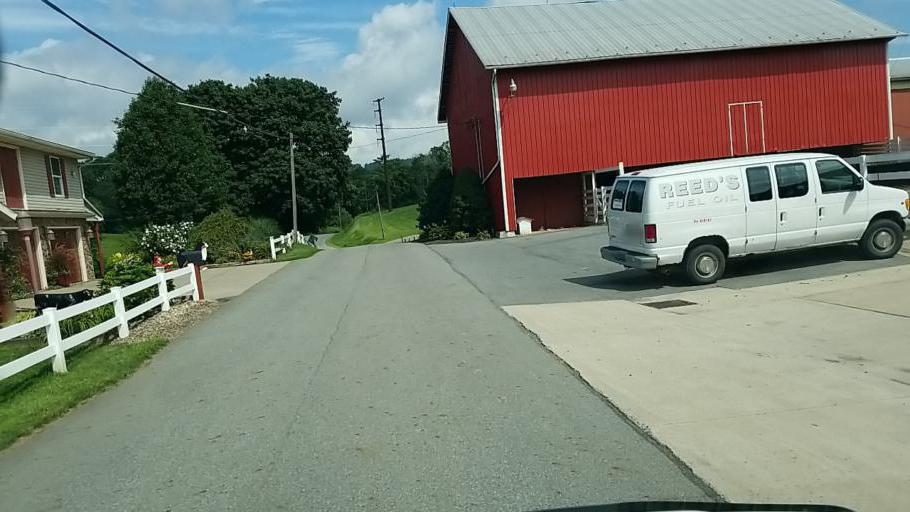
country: US
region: Pennsylvania
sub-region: Dauphin County
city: Millersburg
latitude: 40.5628
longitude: -76.9277
